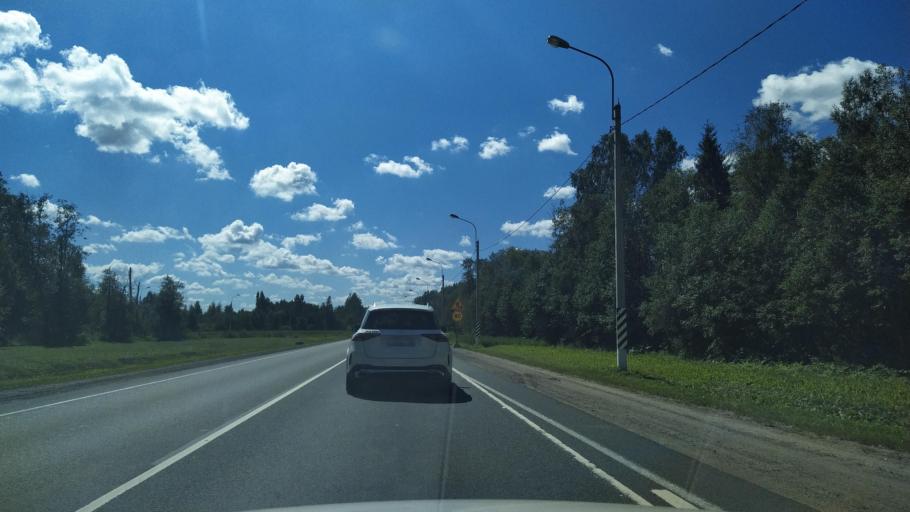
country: RU
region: Leningrad
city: Luga
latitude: 58.6224
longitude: 29.8324
